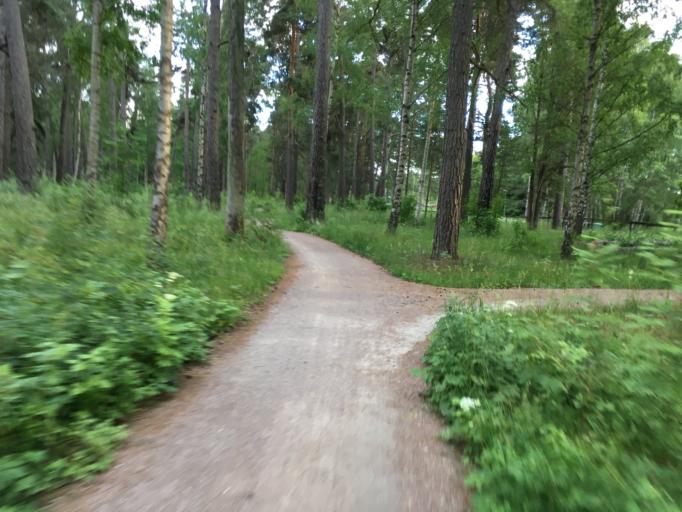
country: SE
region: Uppsala
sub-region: Uppsala Kommun
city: Uppsala
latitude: 59.8370
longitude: 17.6391
